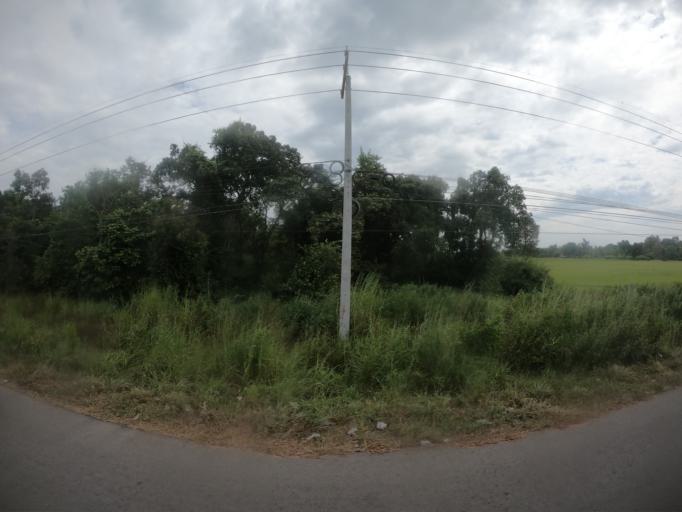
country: TH
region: Maha Sarakham
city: Kantharawichai
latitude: 16.2873
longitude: 103.2936
